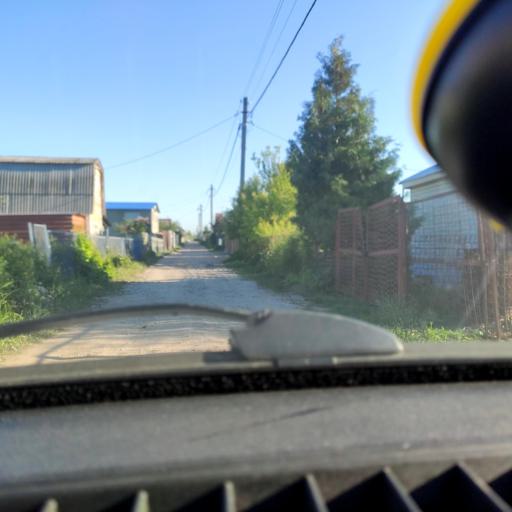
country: RU
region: Samara
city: Tol'yatti
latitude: 53.5944
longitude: 49.3155
